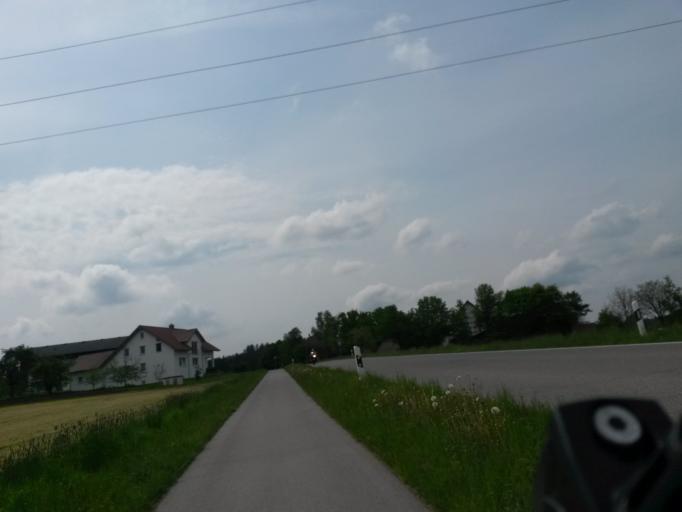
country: DE
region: Baden-Wuerttemberg
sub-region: Tuebingen Region
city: Bad Waldsee
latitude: 47.9570
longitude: 9.7351
